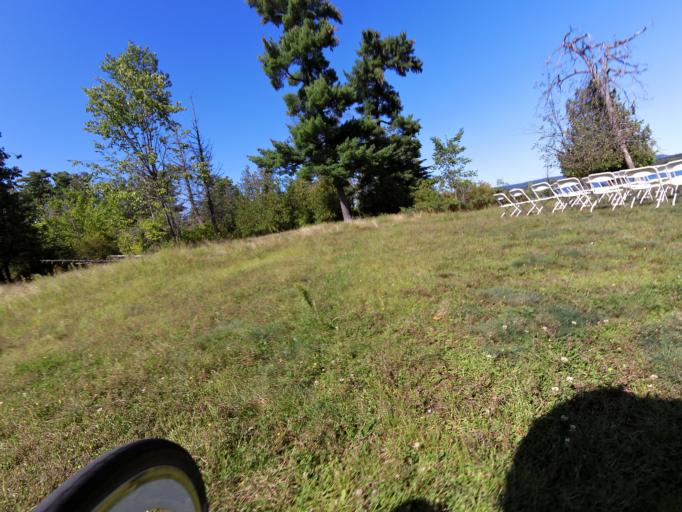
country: CA
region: Ontario
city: Bells Corners
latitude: 45.4429
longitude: -75.9528
